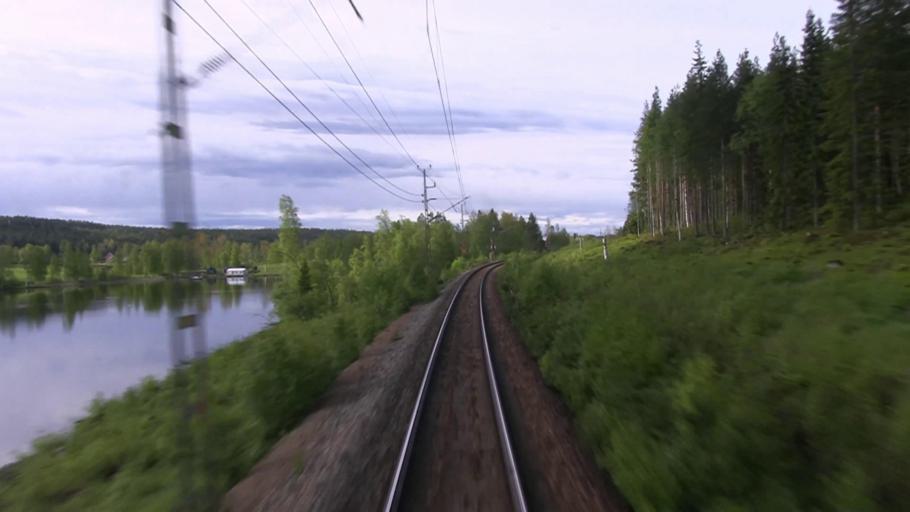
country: SE
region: Vaesterbotten
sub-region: Vindelns Kommun
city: Vindeln
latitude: 64.1121
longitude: 19.6902
